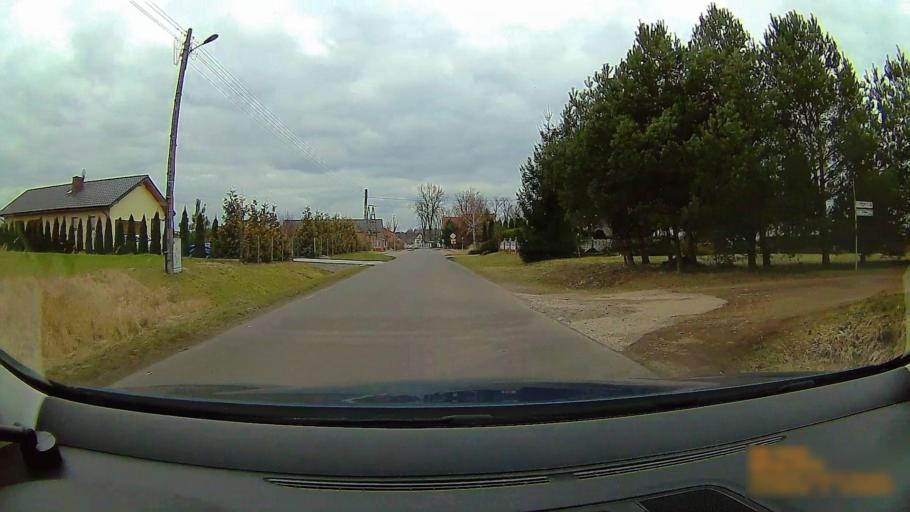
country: PL
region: Greater Poland Voivodeship
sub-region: Powiat koninski
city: Rzgow Pierwszy
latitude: 52.1357
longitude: 18.0569
